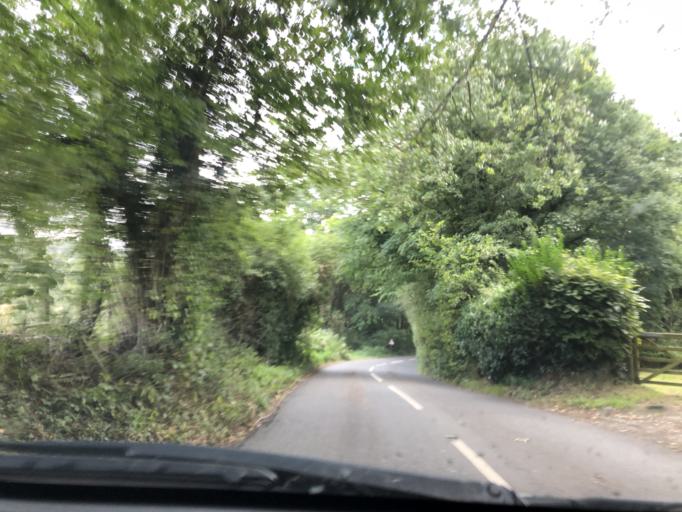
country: GB
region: England
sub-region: Kent
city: Westerham
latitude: 51.2399
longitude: 0.0833
